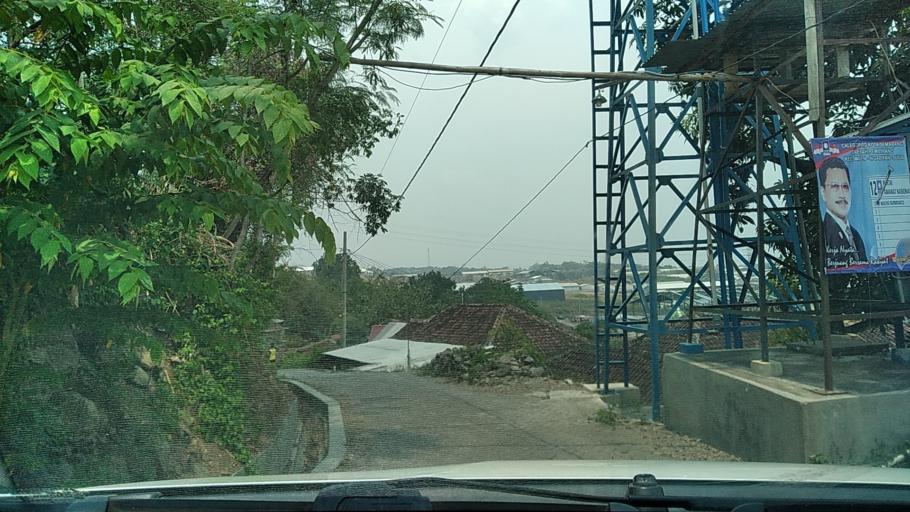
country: ID
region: Central Java
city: Semarang
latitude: -7.0153
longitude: 110.3544
